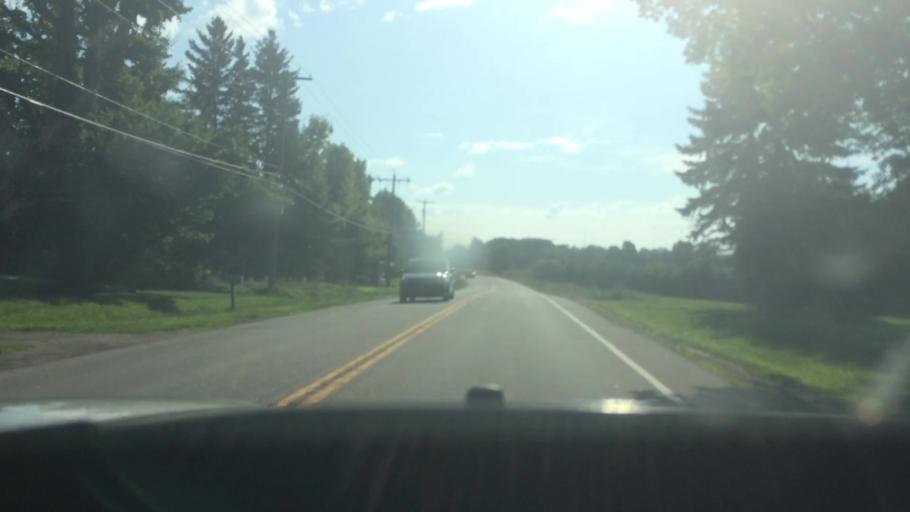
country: US
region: New York
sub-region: Franklin County
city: Malone
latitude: 44.7974
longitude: -74.4583
